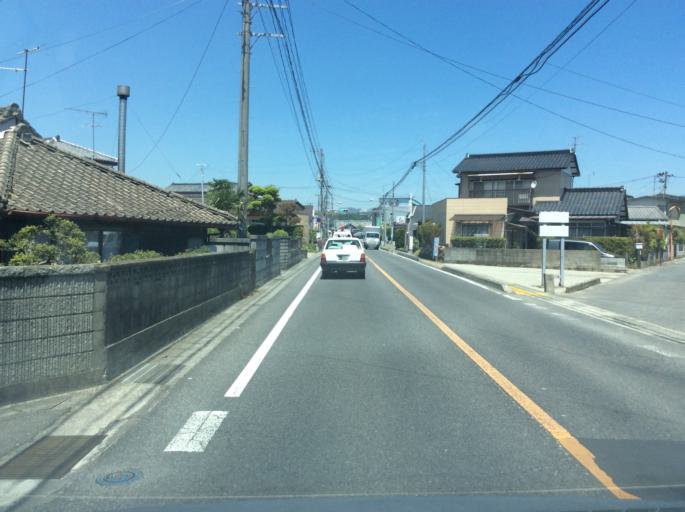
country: JP
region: Fukushima
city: Iwaki
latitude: 37.0811
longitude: 140.8794
